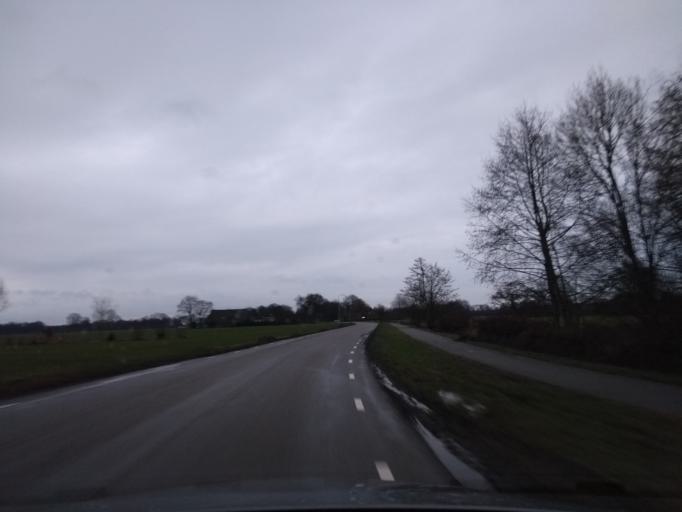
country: NL
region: Drenthe
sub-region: Gemeente De Wolden
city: Ruinen
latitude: 52.6727
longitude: 6.3204
